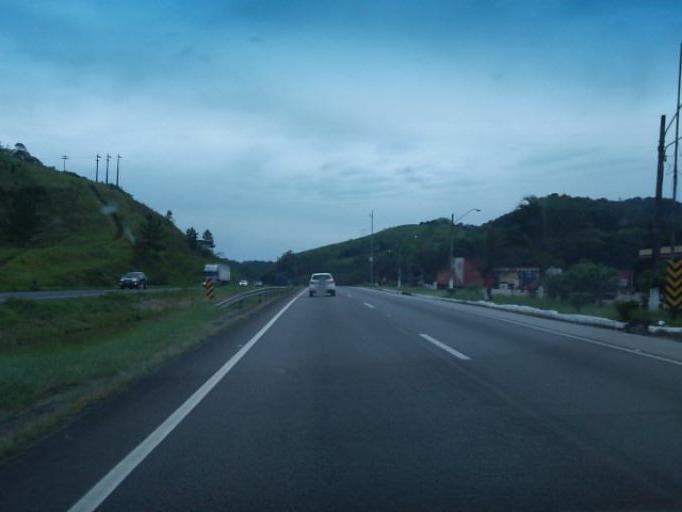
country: BR
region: Sao Paulo
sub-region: Juquia
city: Juquia
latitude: -24.3618
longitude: -47.6899
